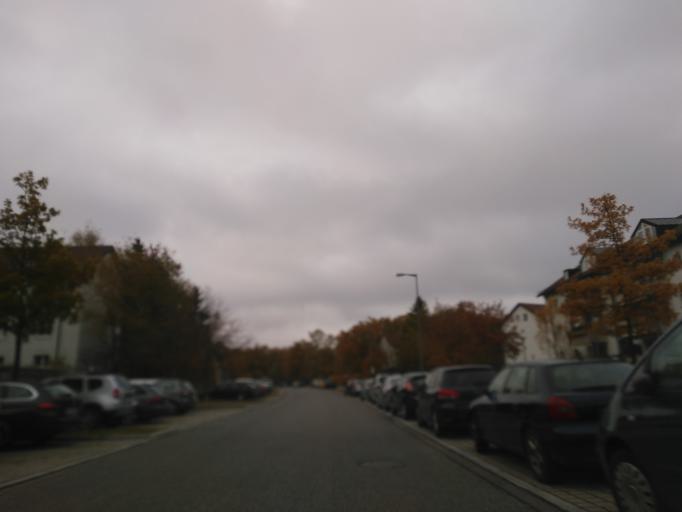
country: DE
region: Bavaria
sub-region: Upper Bavaria
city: Unterhaching
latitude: 48.0893
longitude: 11.5985
